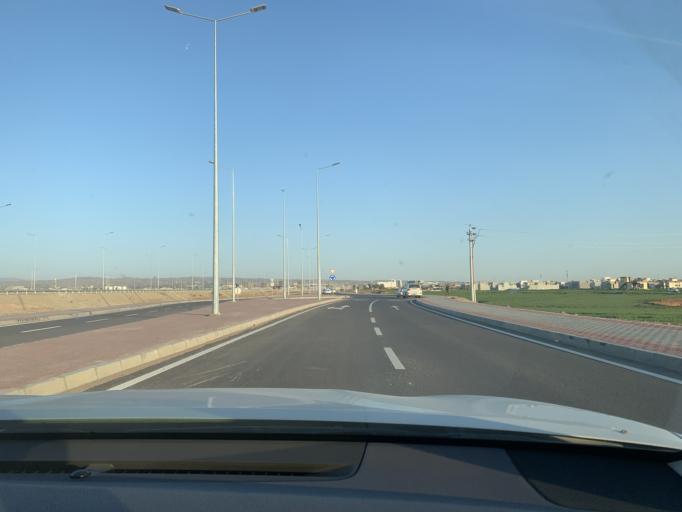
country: IQ
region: Arbil
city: Erbil
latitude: 36.2828
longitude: 44.0564
